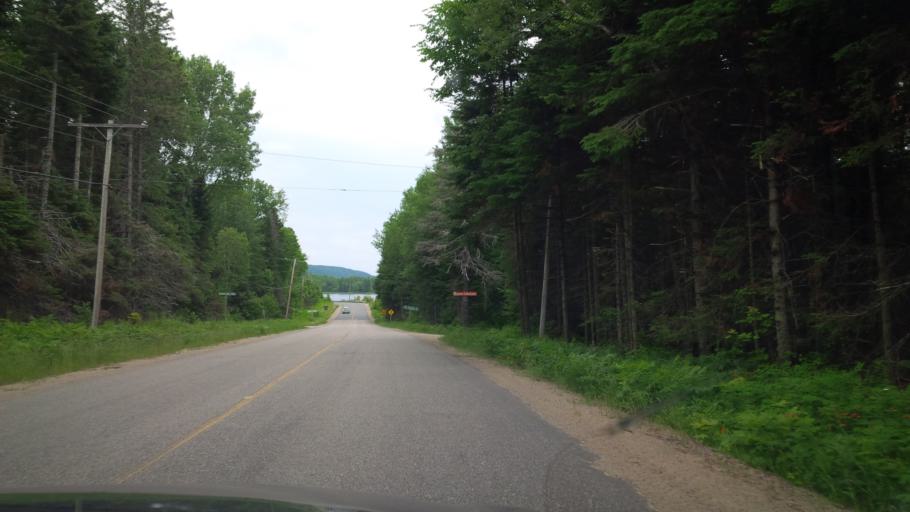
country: CA
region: Ontario
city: Huntsville
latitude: 45.5769
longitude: -79.2171
